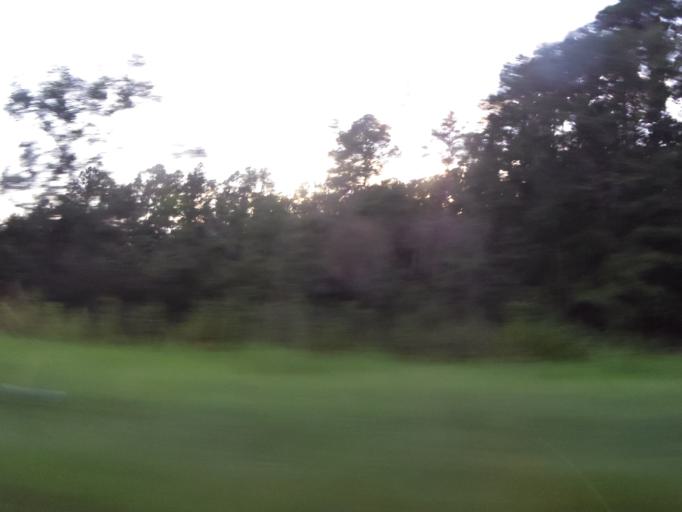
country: US
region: Georgia
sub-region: Camden County
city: Kingsland
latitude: 30.8338
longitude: -81.6971
